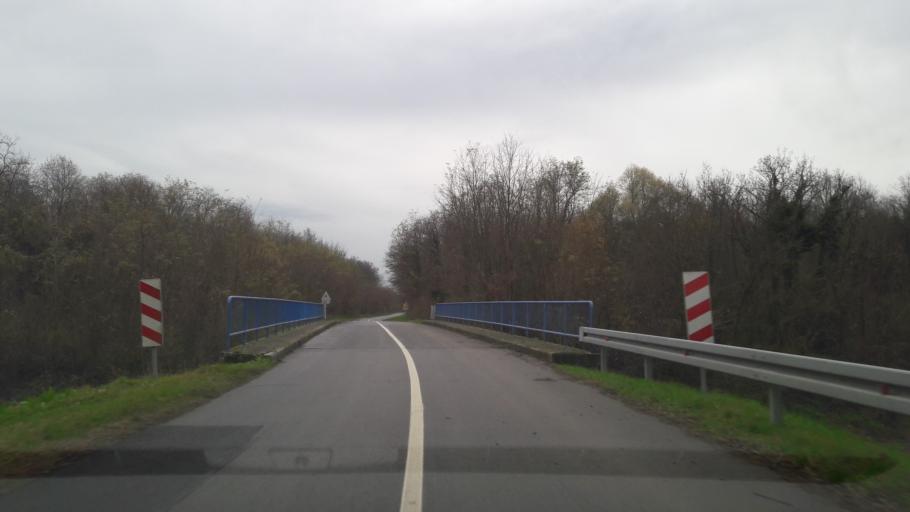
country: HR
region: Osjecko-Baranjska
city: Koska
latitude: 45.5898
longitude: 18.2366
